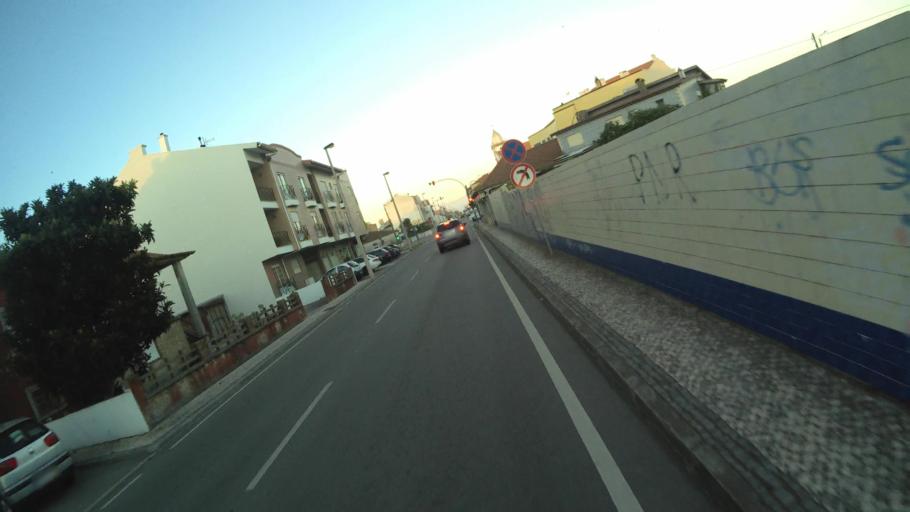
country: PT
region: Aveiro
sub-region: Ilhavo
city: Gafanha da Nazare
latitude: 40.6375
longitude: -8.7164
